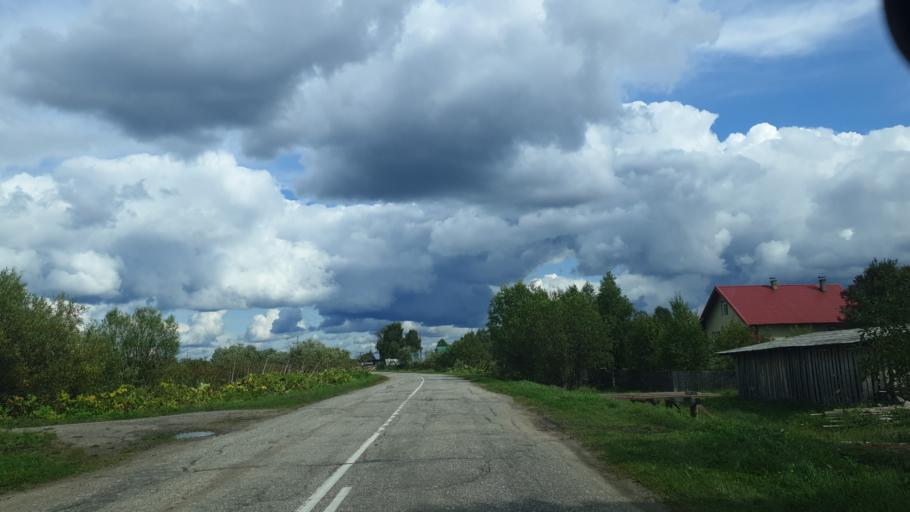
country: RU
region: Komi Republic
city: Aykino
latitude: 61.9529
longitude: 50.1755
